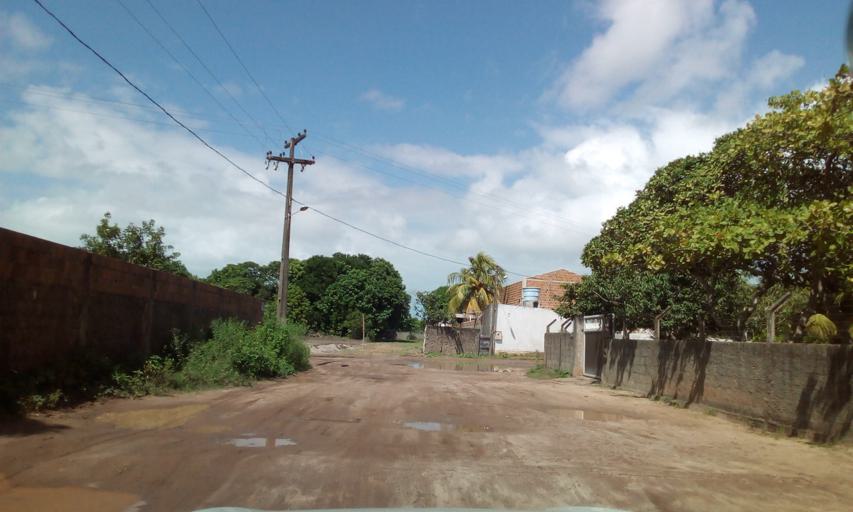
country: BR
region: Paraiba
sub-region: Conde
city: Conde
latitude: -7.2225
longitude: -34.8228
